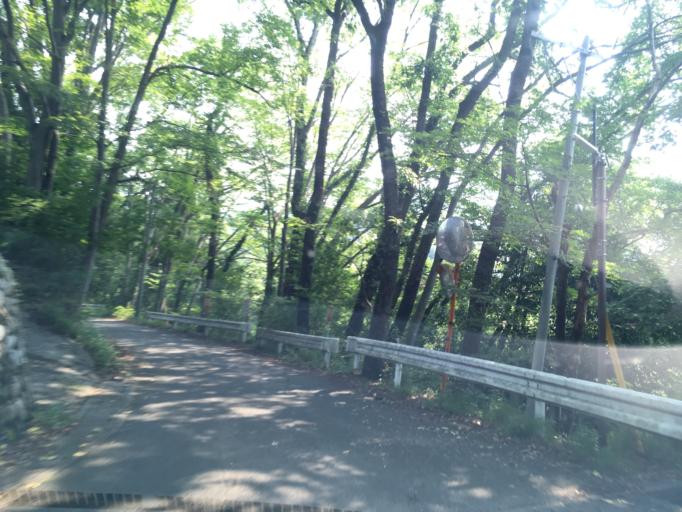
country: JP
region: Saitama
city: Chichibu
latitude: 36.0009
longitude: 139.1037
